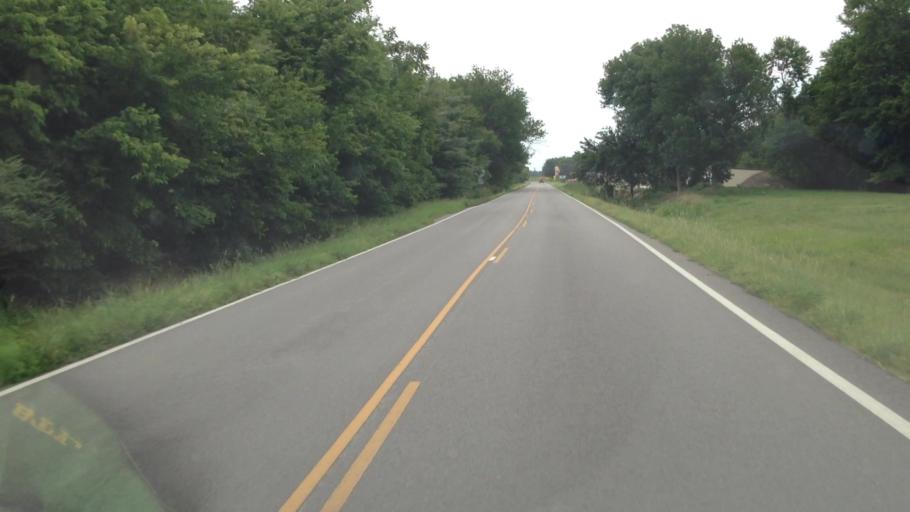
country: US
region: Oklahoma
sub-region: Delaware County
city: Cleora
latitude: 36.5686
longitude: -94.9753
